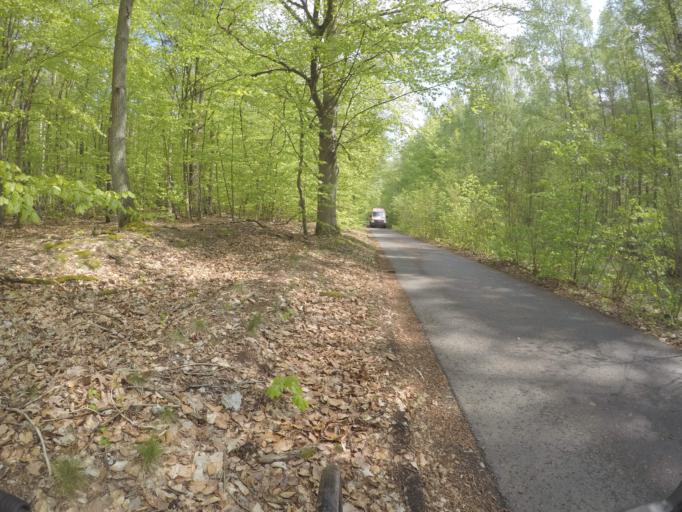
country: DE
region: Brandenburg
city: Marienwerder
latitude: 52.8535
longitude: 13.6082
